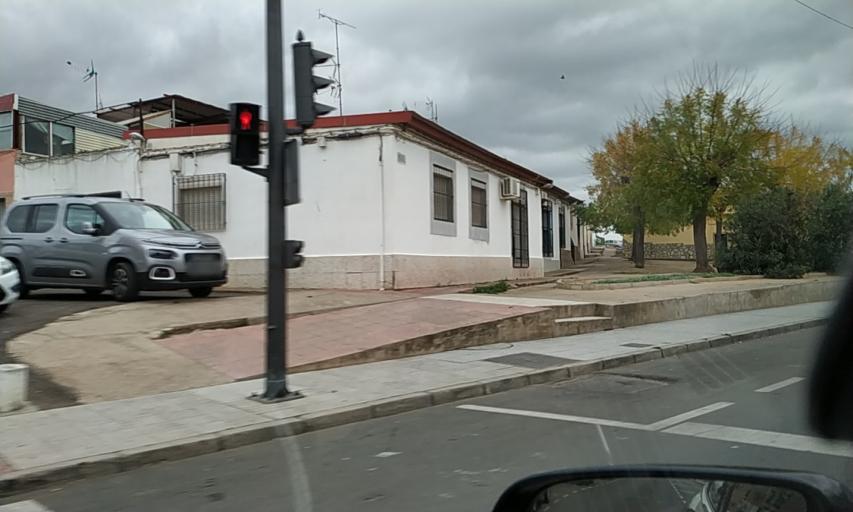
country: ES
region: Extremadura
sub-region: Provincia de Badajoz
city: Badajoz
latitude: 38.8908
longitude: -6.9774
